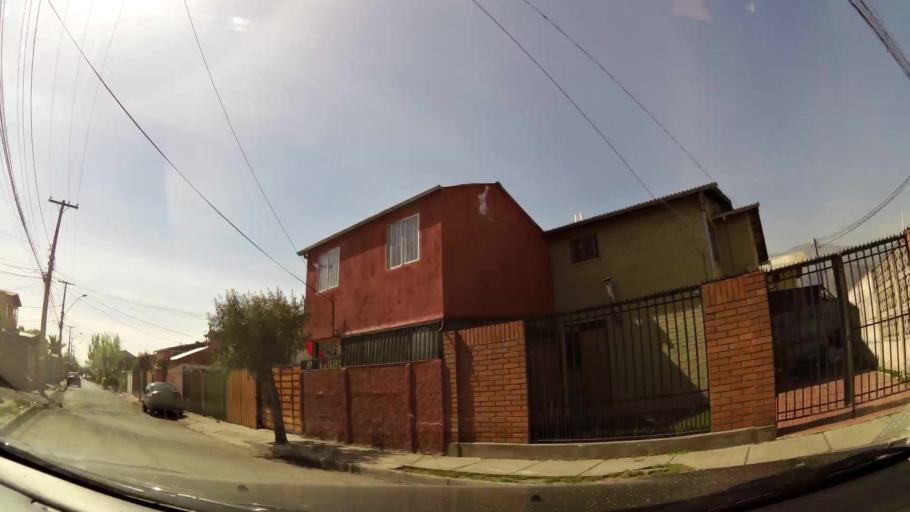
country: CL
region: Santiago Metropolitan
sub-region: Provincia de Cordillera
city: Puente Alto
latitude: -33.5643
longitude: -70.5630
